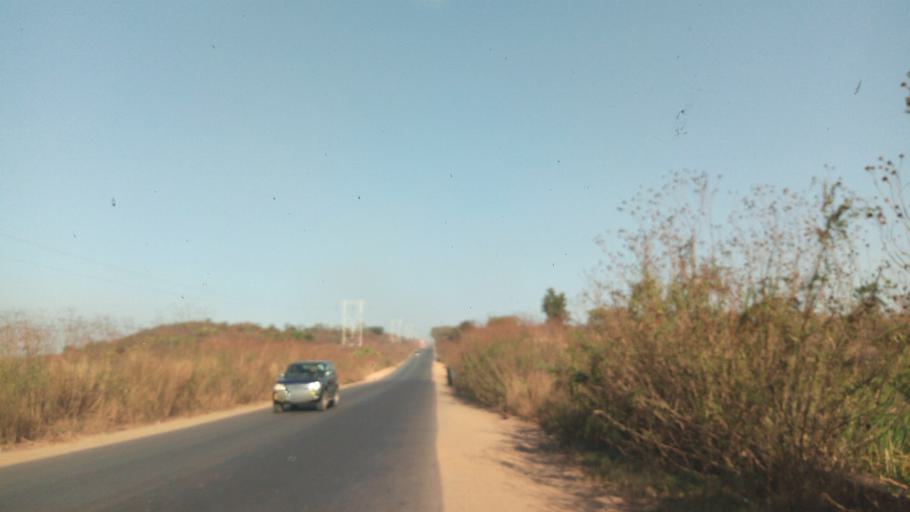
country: CD
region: Katanga
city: Likasi
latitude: -11.0546
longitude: 26.9631
